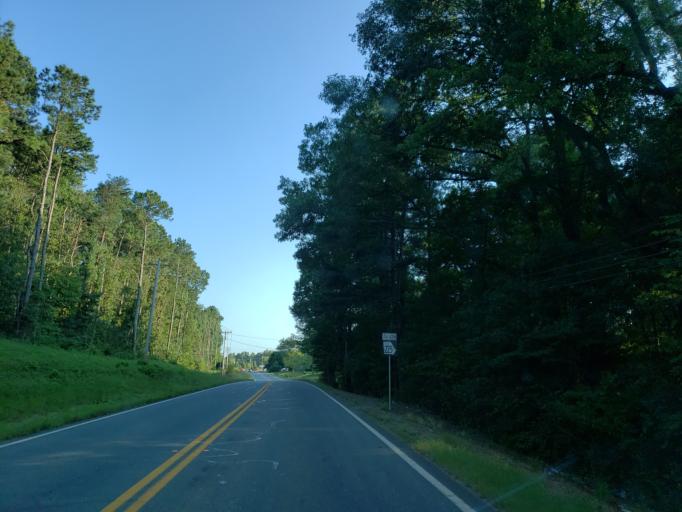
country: US
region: Georgia
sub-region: Murray County
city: Chatsworth
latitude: 34.7333
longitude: -84.8206
